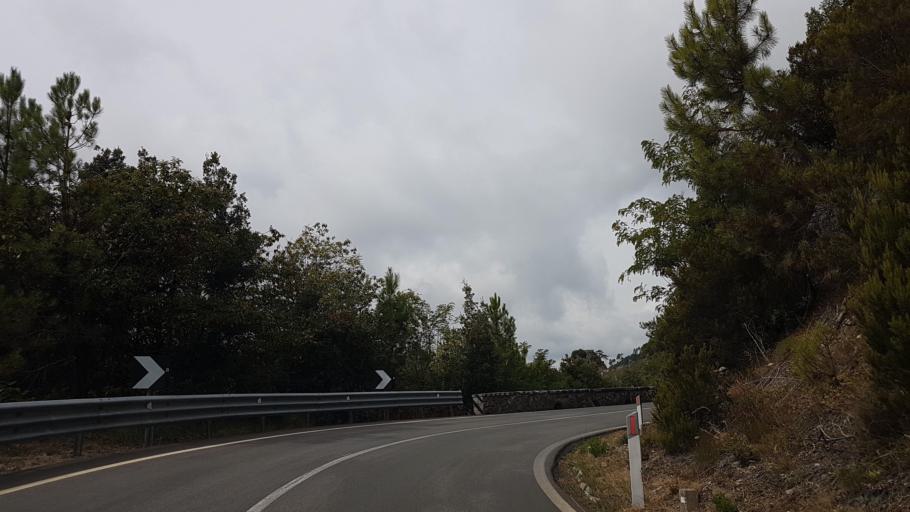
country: IT
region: Liguria
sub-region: Provincia di La Spezia
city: Framura
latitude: 44.2483
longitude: 9.5719
